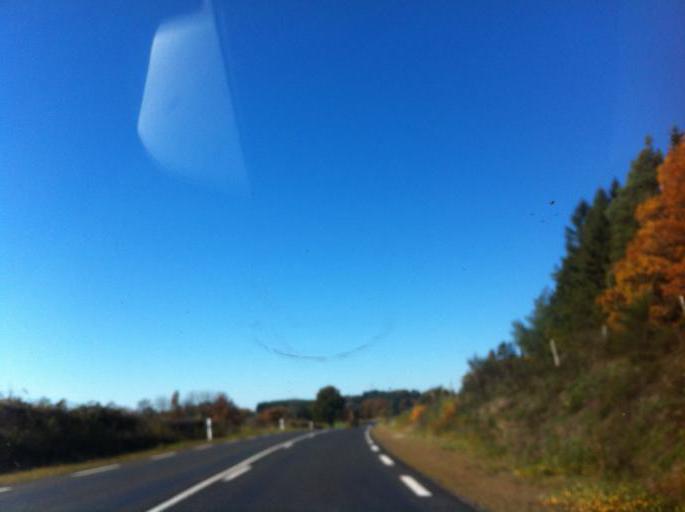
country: FR
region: Auvergne
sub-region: Departement du Puy-de-Dome
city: Gelles
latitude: 45.8615
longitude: 2.6390
